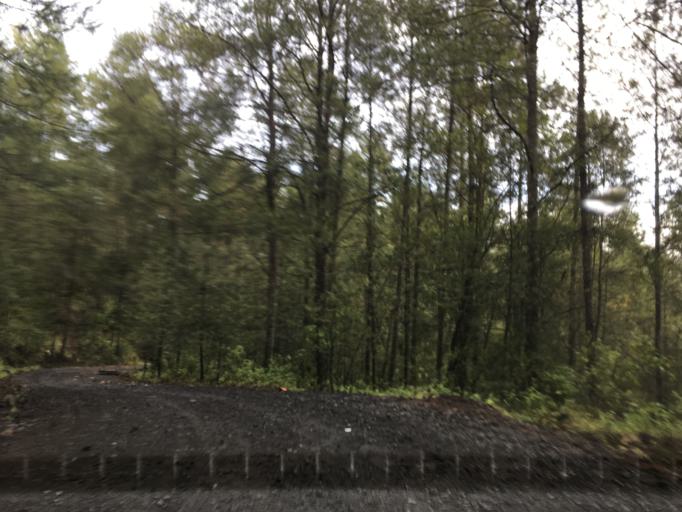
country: MX
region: Michoacan
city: Angahuan
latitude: 19.4833
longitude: -102.2067
